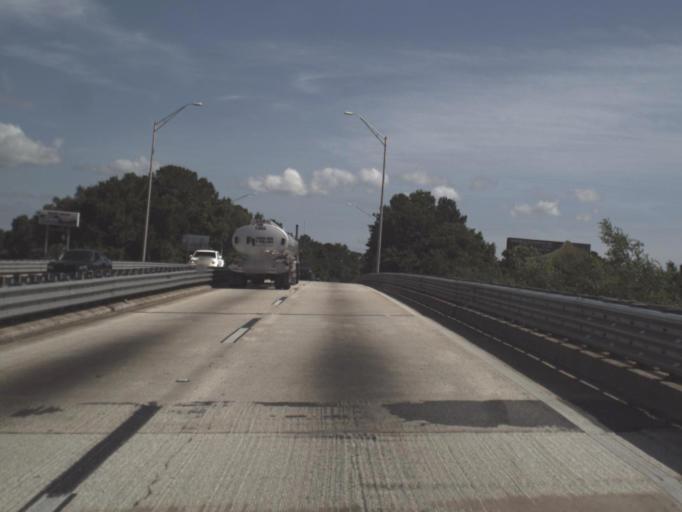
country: US
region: Florida
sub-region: Duval County
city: Jacksonville
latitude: 30.3129
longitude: -81.7040
